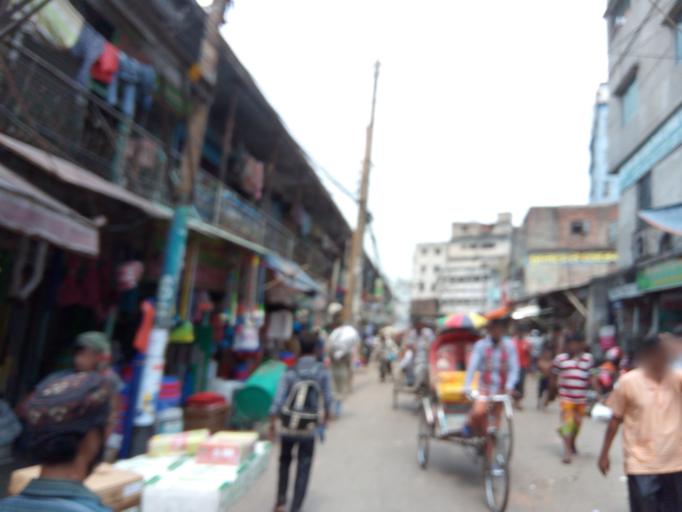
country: BD
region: Dhaka
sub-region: Dhaka
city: Dhaka
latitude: 23.7221
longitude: 90.4134
